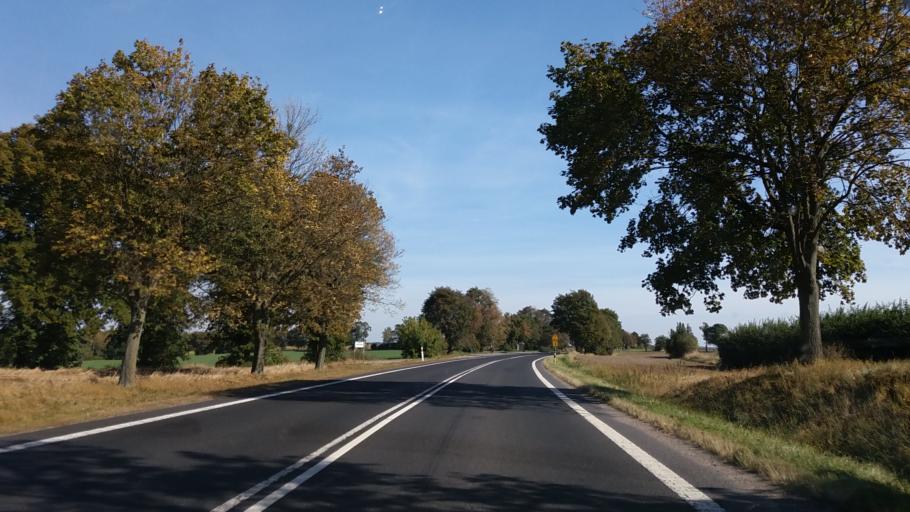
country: PL
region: Greater Poland Voivodeship
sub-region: Powiat miedzychodzki
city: Kwilcz
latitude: 52.5646
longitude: 16.0253
